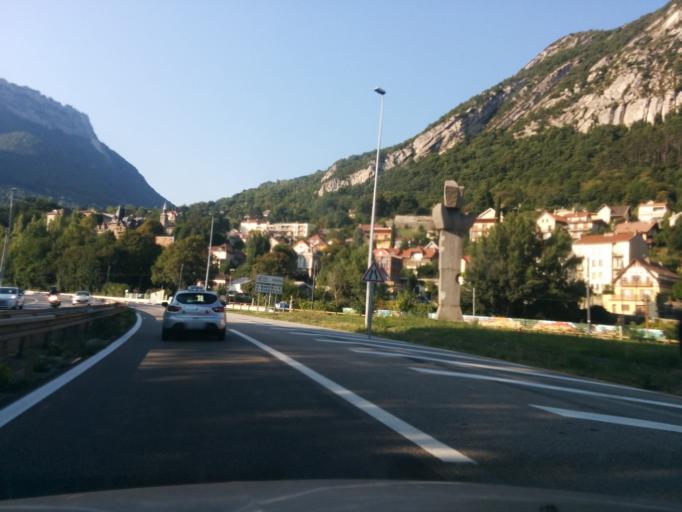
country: FR
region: Rhone-Alpes
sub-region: Departement de l'Isere
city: Saint-Martin-le-Vinoux
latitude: 45.1994
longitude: 5.7165
